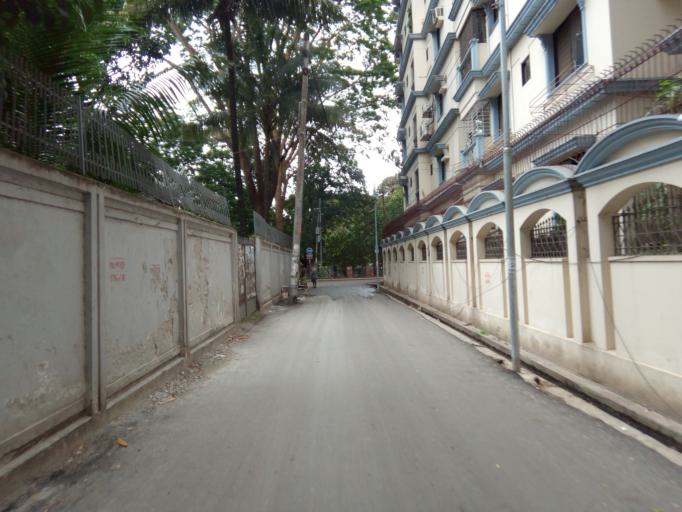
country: BD
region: Dhaka
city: Azimpur
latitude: 23.7483
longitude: 90.3775
